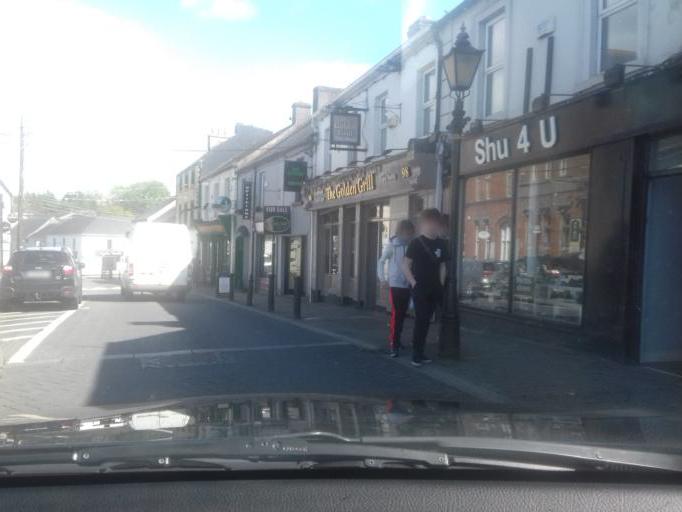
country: IE
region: Leinster
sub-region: Laois
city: Portlaoise
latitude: 53.0340
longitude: -7.2969
